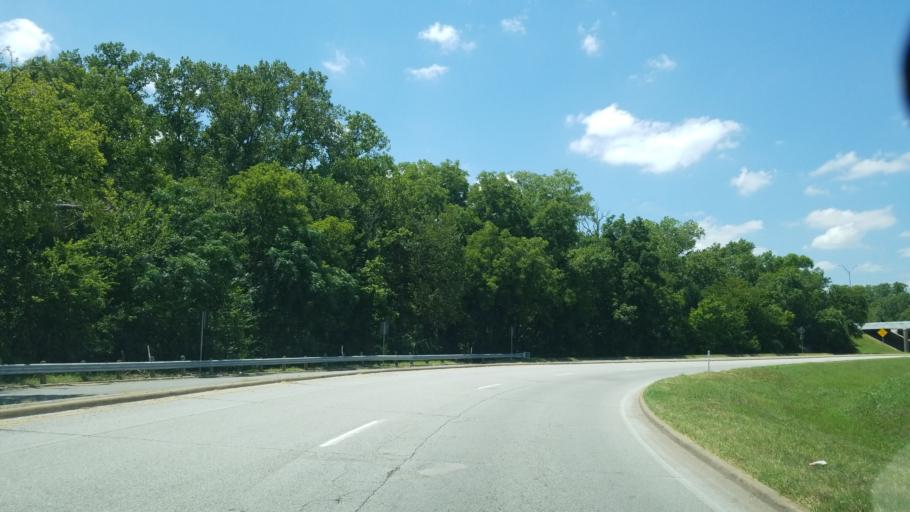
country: US
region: Texas
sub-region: Dallas County
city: Dallas
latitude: 32.7437
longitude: -96.7264
